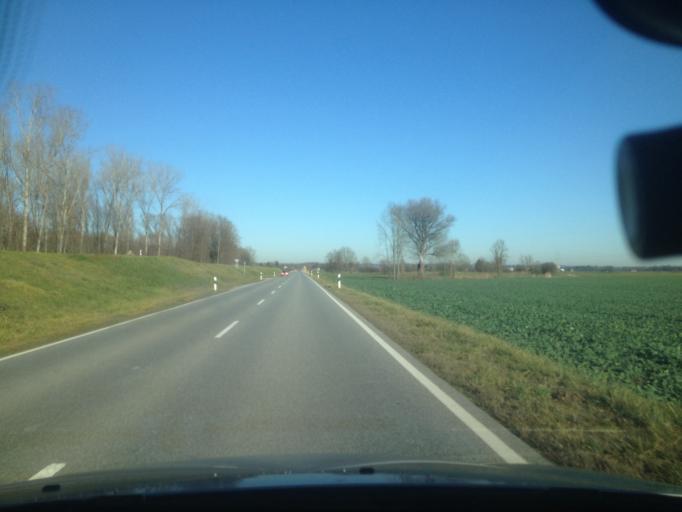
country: DE
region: Bavaria
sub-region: Upper Bavaria
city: Moosburg
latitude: 48.4513
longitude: 11.9473
